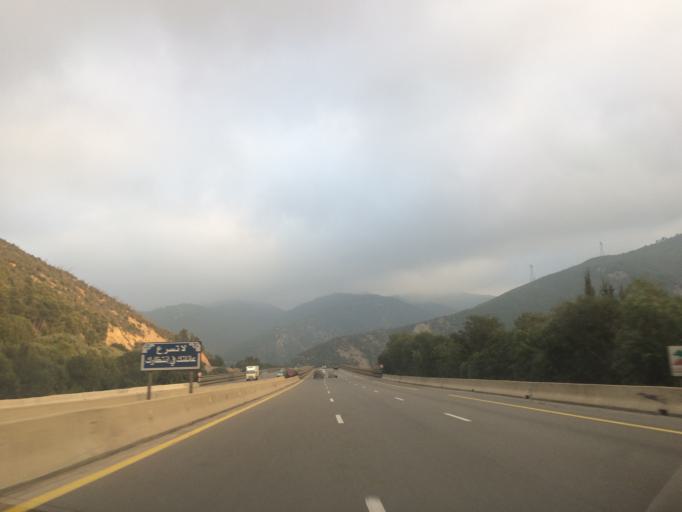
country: DZ
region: Tipaza
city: El Affroun
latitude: 36.4028
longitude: 2.5465
